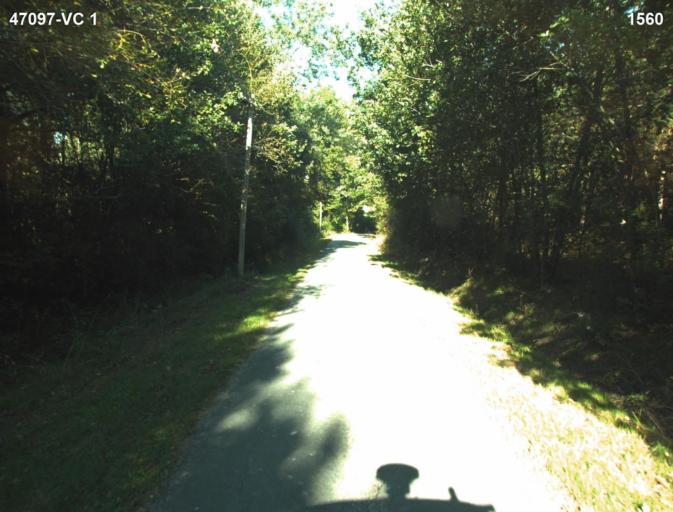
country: FR
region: Aquitaine
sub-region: Departement du Lot-et-Garonne
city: Vianne
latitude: 44.2110
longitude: 0.3574
